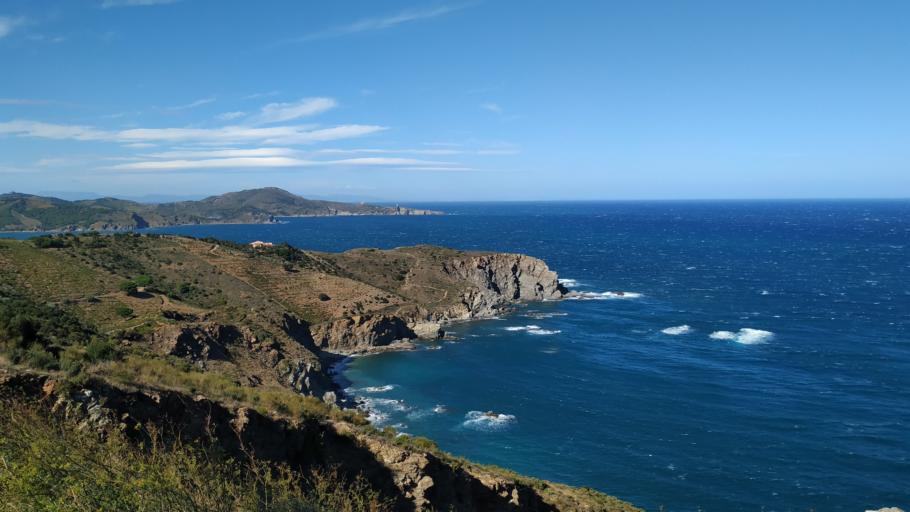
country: FR
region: Languedoc-Roussillon
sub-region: Departement des Pyrenees-Orientales
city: Cervera de la Marenda
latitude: 42.4676
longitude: 3.1565
